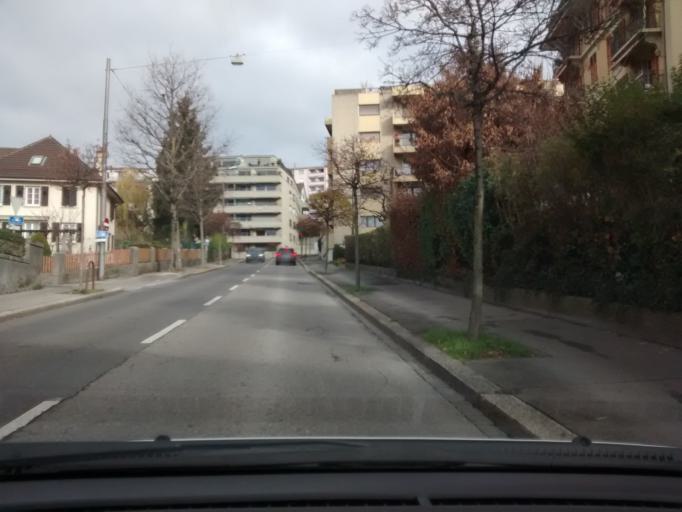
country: CH
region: Vaud
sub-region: Lausanne District
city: Blecherette
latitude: 46.5251
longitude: 6.6167
